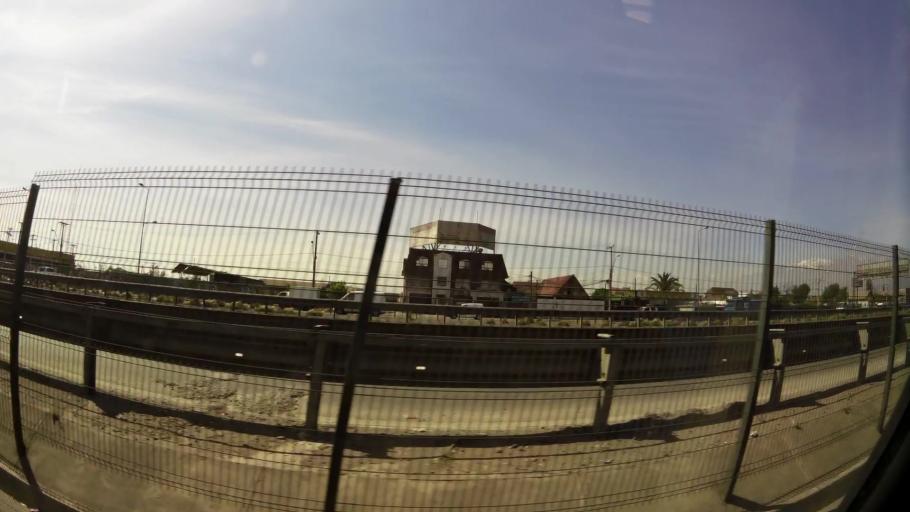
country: CL
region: Santiago Metropolitan
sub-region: Provincia de Maipo
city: San Bernardo
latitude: -33.5334
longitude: -70.6779
